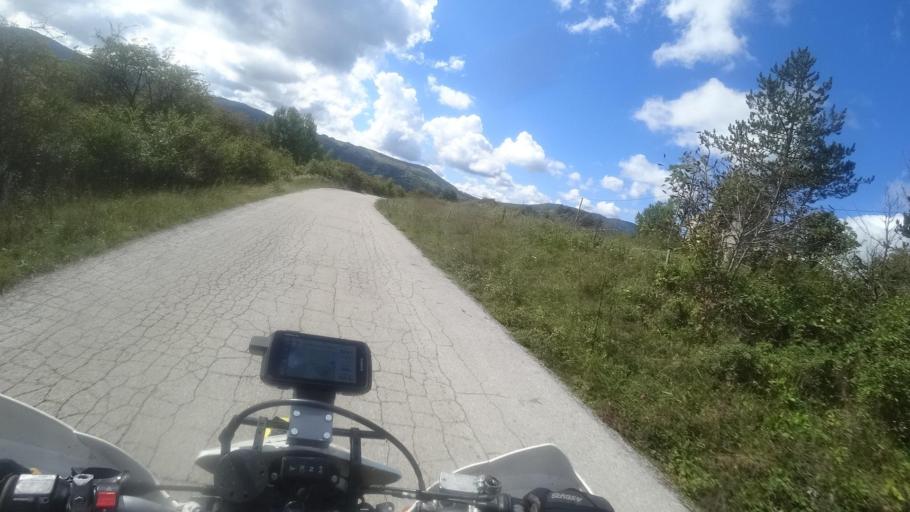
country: BA
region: Federation of Bosnia and Herzegovina
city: Bosanska Krupa
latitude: 44.8475
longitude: 16.0719
